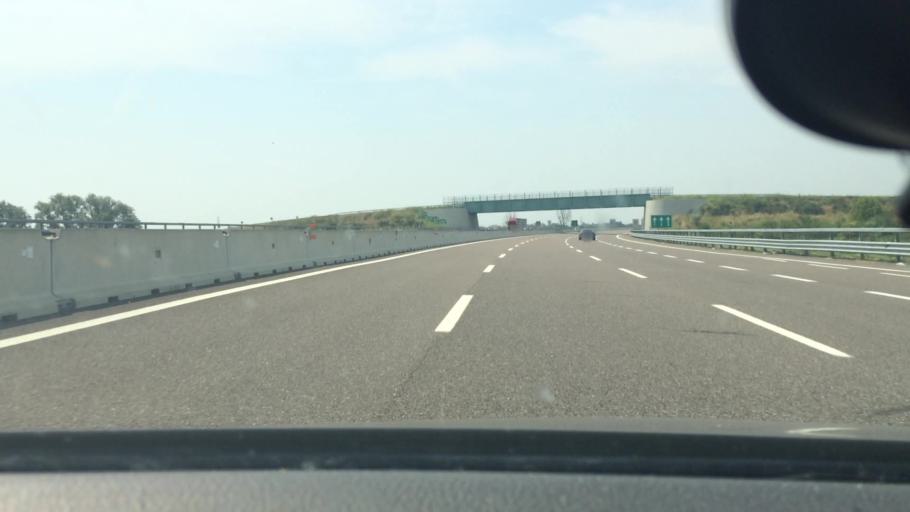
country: IT
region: Lombardy
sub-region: Citta metropolitana di Milano
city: Pozzuolo Martesana
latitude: 45.4951
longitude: 9.4441
